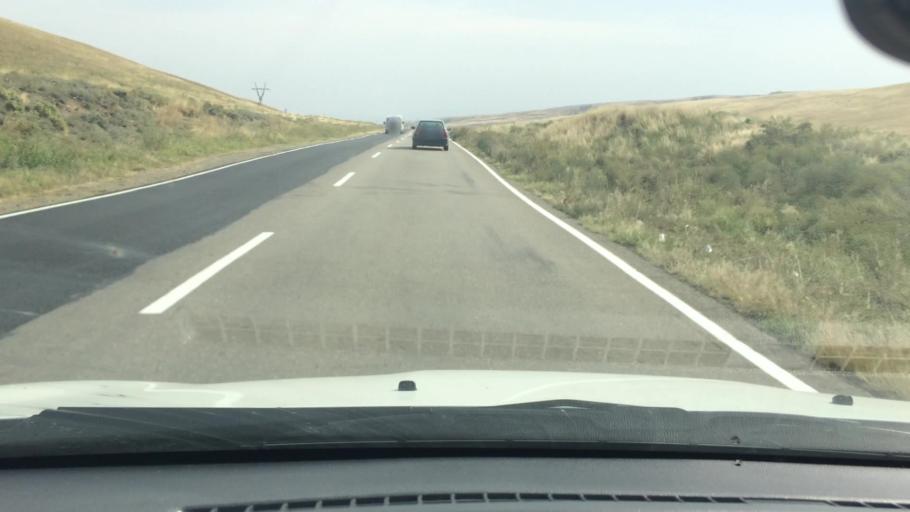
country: GE
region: Kvemo Kartli
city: Rust'avi
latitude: 41.5130
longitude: 44.9467
